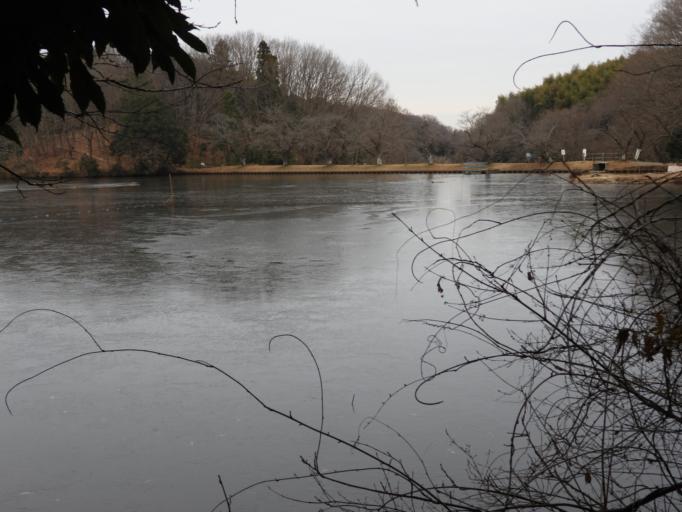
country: JP
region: Ibaraki
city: Naka
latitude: 36.0800
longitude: 140.1640
